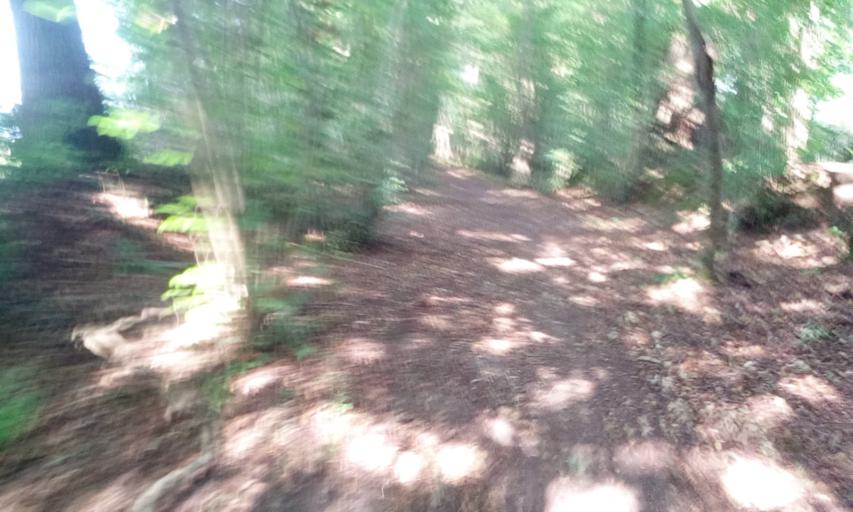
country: FR
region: Lower Normandy
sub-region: Departement du Calvados
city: Argences
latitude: 49.1425
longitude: -0.1101
